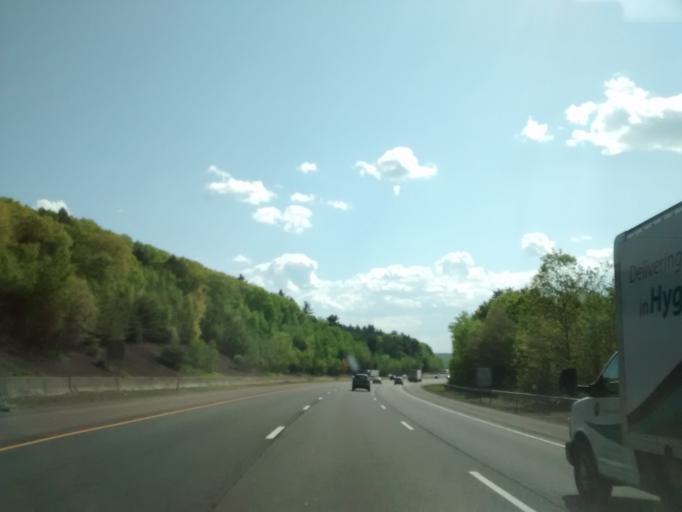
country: US
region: Connecticut
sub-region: Tolland County
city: Stafford Springs
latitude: 41.9053
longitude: -72.2759
